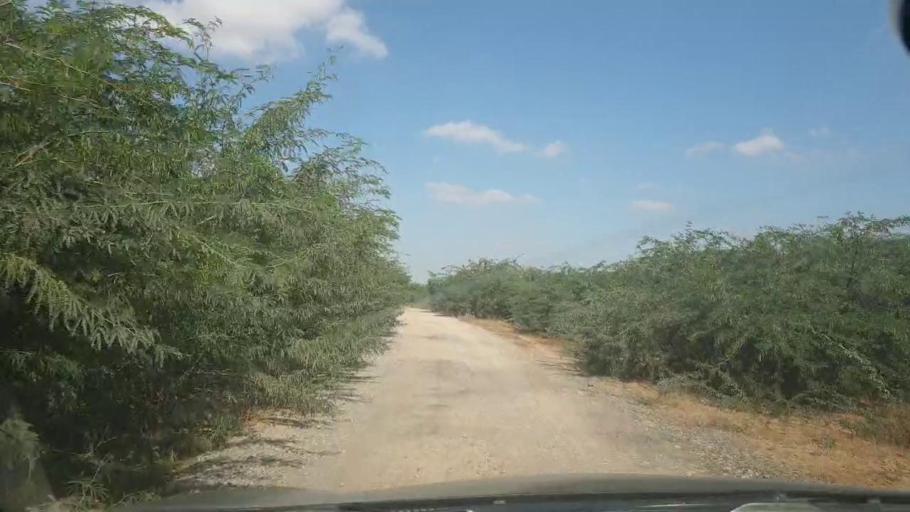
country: PK
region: Sindh
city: Malir Cantonment
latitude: 25.0623
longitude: 67.3958
